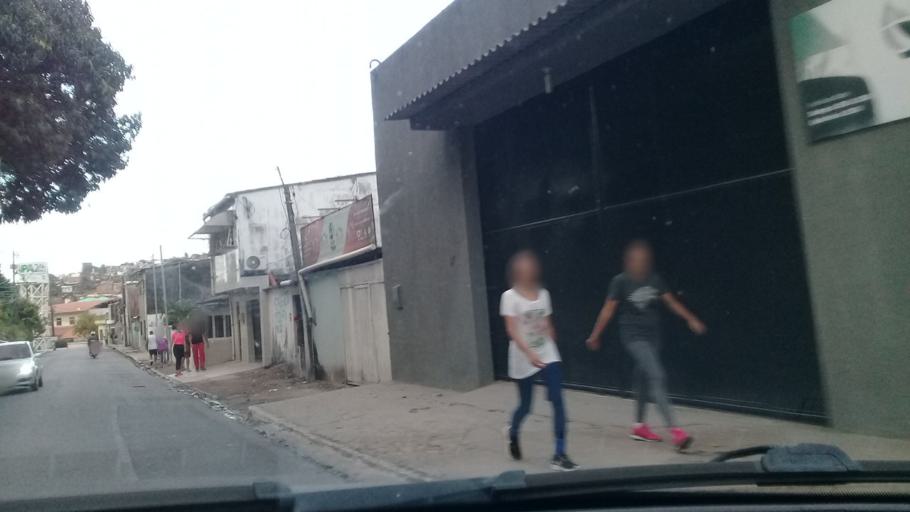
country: BR
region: Pernambuco
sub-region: Jaboatao Dos Guararapes
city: Jaboatao dos Guararapes
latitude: -8.1303
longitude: -34.9496
